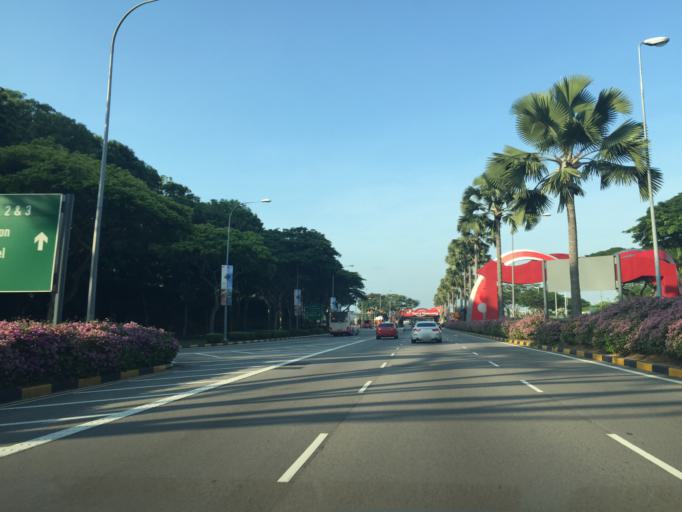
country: SG
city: Singapore
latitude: 1.3496
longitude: 103.9853
